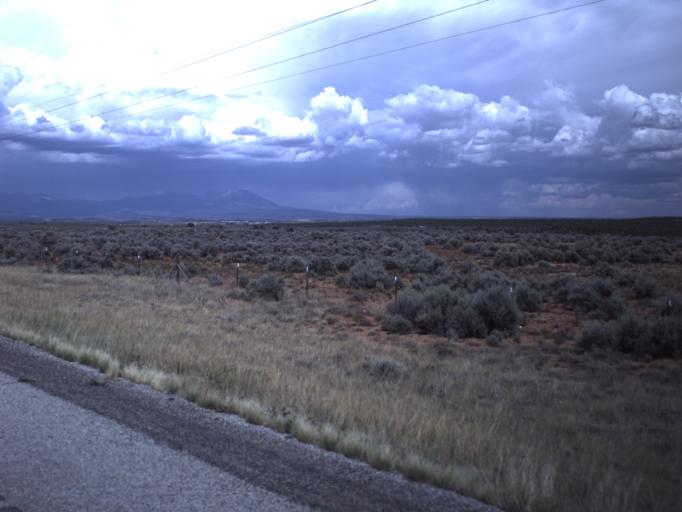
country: US
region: Utah
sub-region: San Juan County
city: Blanding
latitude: 37.5085
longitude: -109.4906
